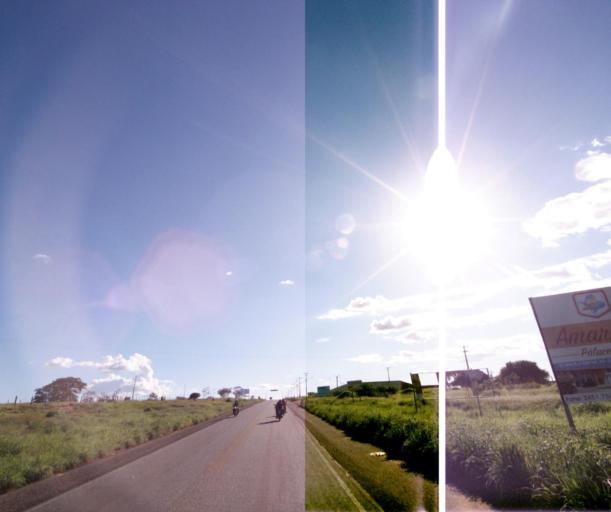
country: BR
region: Bahia
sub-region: Guanambi
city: Guanambi
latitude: -14.1966
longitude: -42.7504
